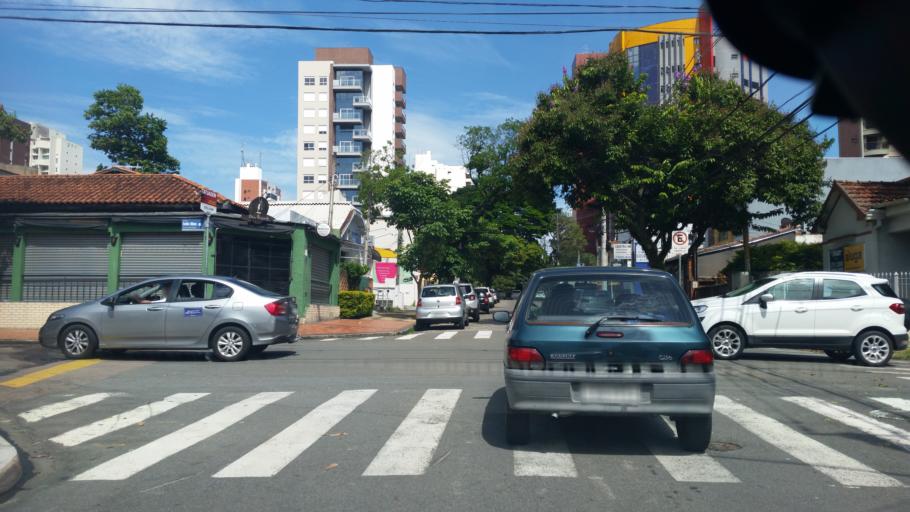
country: BR
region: Sao Paulo
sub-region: Campinas
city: Campinas
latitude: -22.8920
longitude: -47.0508
